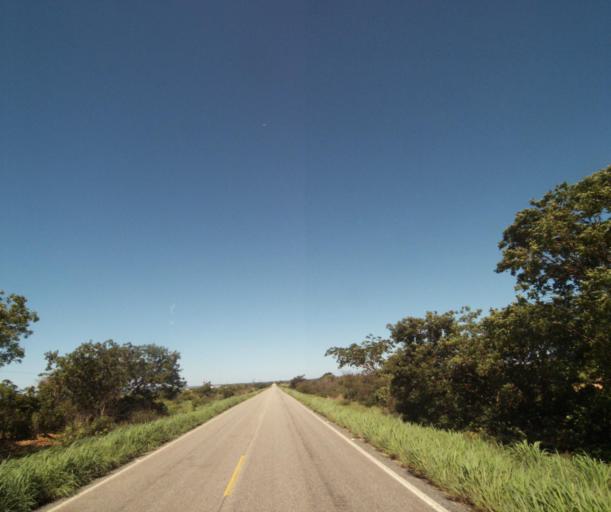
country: BR
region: Bahia
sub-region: Palmas De Monte Alto
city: Palmas de Monte Alto
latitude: -14.2562
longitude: -43.2453
